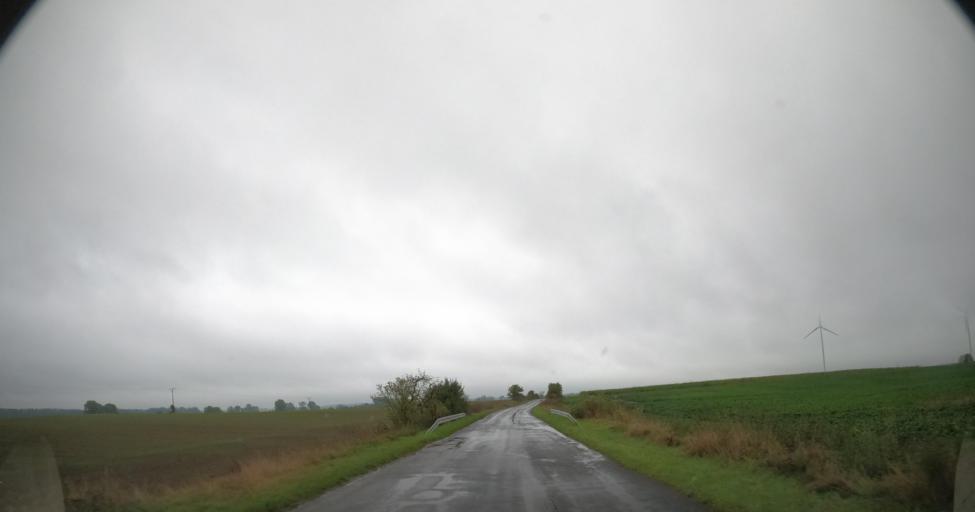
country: PL
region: West Pomeranian Voivodeship
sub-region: Powiat pyrzycki
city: Kozielice
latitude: 53.0614
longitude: 14.7820
